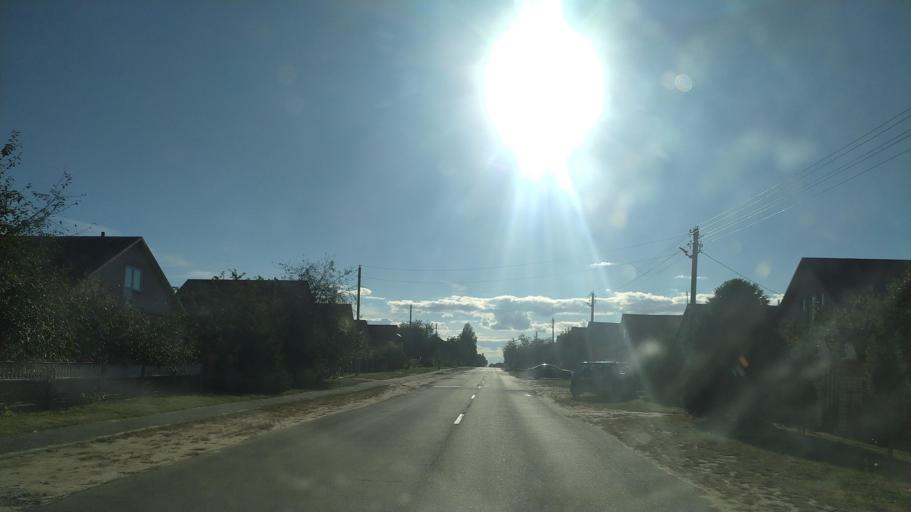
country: BY
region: Brest
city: Byaroza
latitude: 52.5472
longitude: 24.9790
